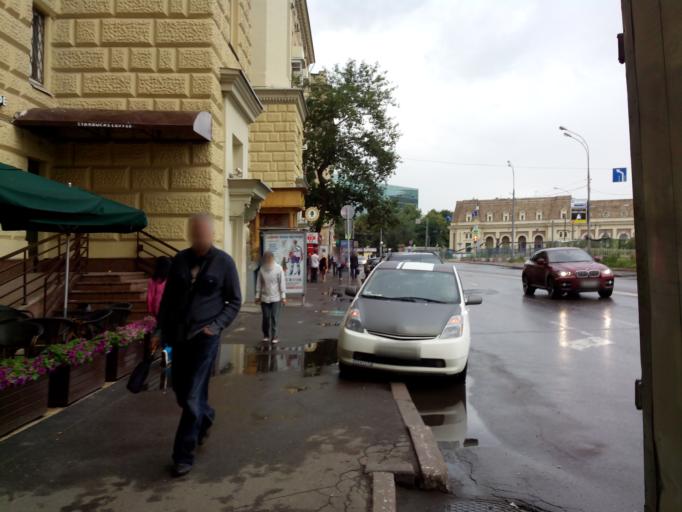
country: RU
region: Moscow
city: Zamoskvorech'ye
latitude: 55.7317
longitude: 37.6405
